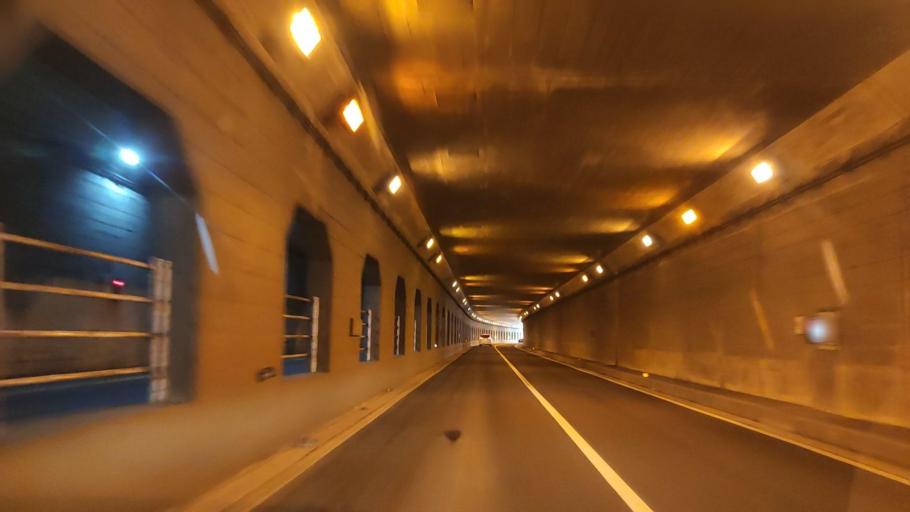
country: JP
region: Miyagi
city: Shiogama
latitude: 38.3032
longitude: 141.0220
